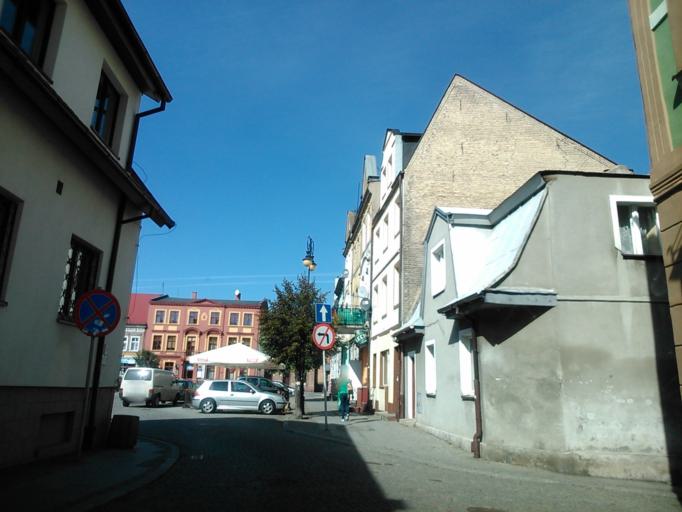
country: PL
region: Kujawsko-Pomorskie
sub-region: Powiat golubsko-dobrzynski
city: Golub-Dobrzyn
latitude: 53.1137
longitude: 19.0554
